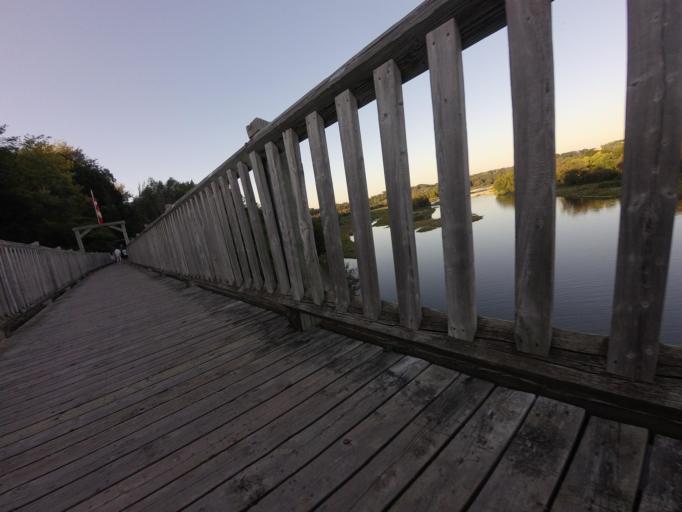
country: CA
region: Ontario
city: Goderich
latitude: 43.7522
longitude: -81.7140
